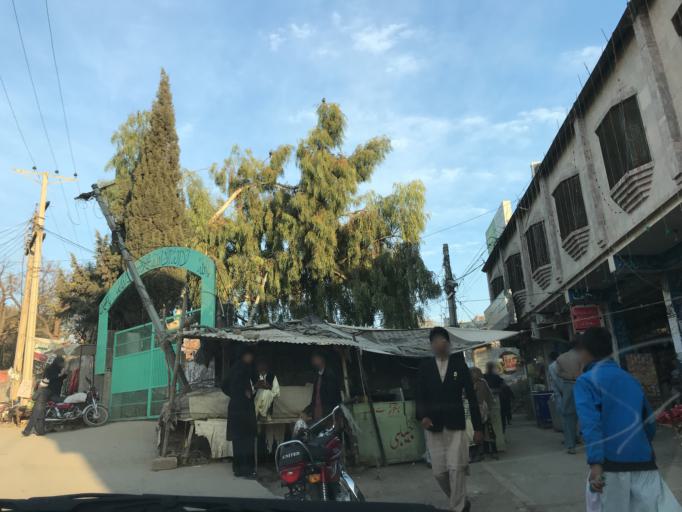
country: PK
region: Islamabad
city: Islamabad
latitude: 33.6924
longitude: 72.9764
